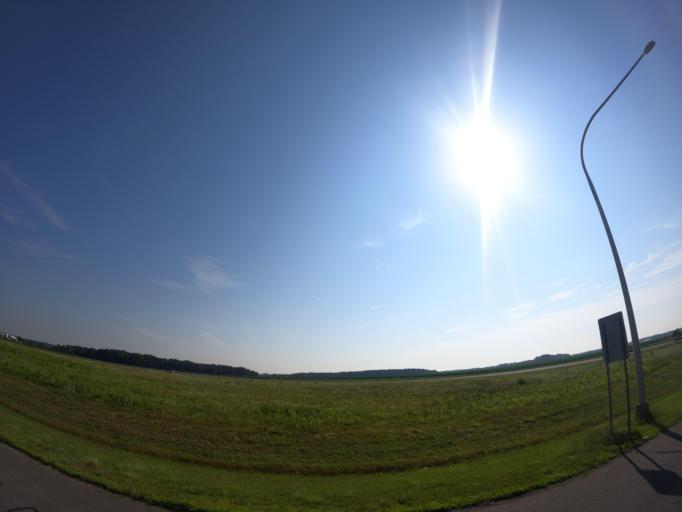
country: US
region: Delaware
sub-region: Sussex County
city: Bridgeville
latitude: 38.7215
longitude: -75.5871
